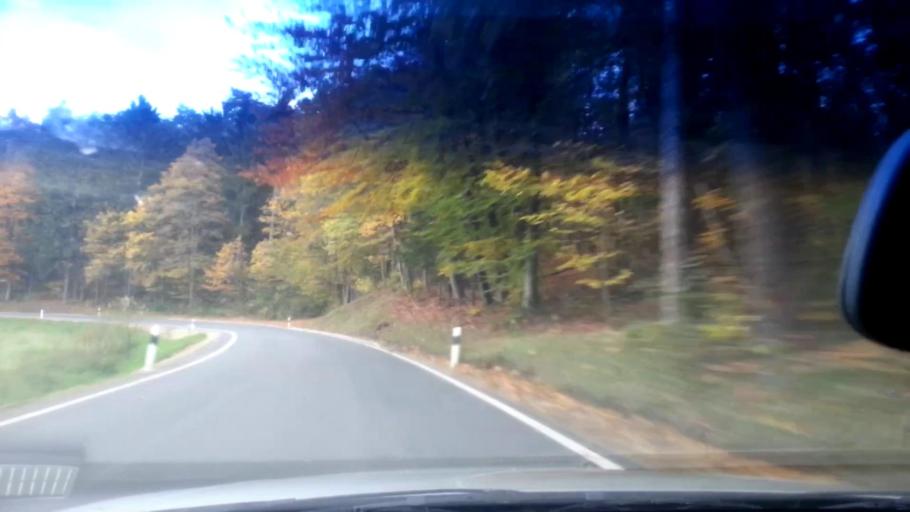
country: DE
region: Bavaria
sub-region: Upper Franconia
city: Wonsees
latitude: 49.9852
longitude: 11.2961
